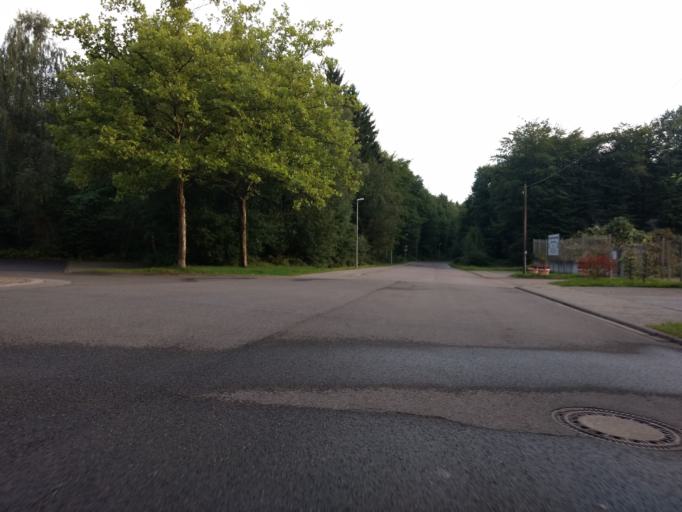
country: DE
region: Saarland
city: Dillingen
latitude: 49.3801
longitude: 6.7300
